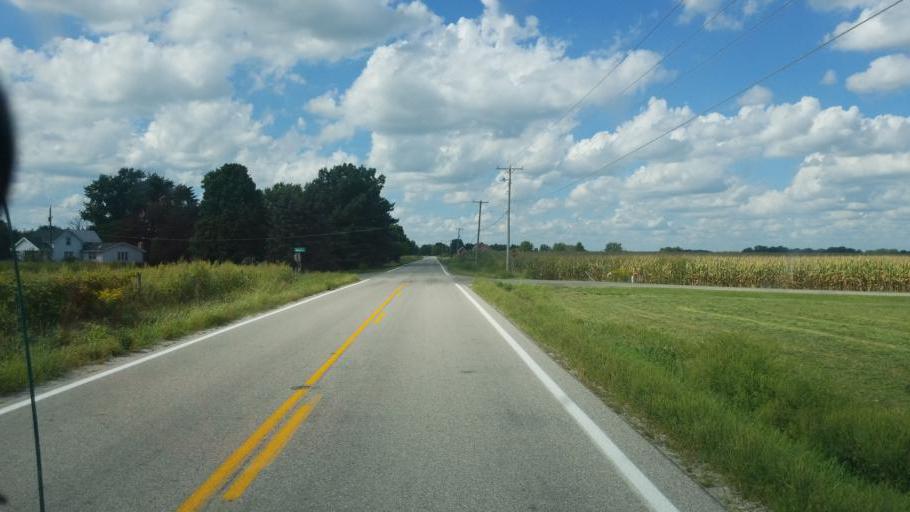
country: US
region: Ohio
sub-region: Union County
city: Richwood
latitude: 40.3638
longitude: -83.2623
